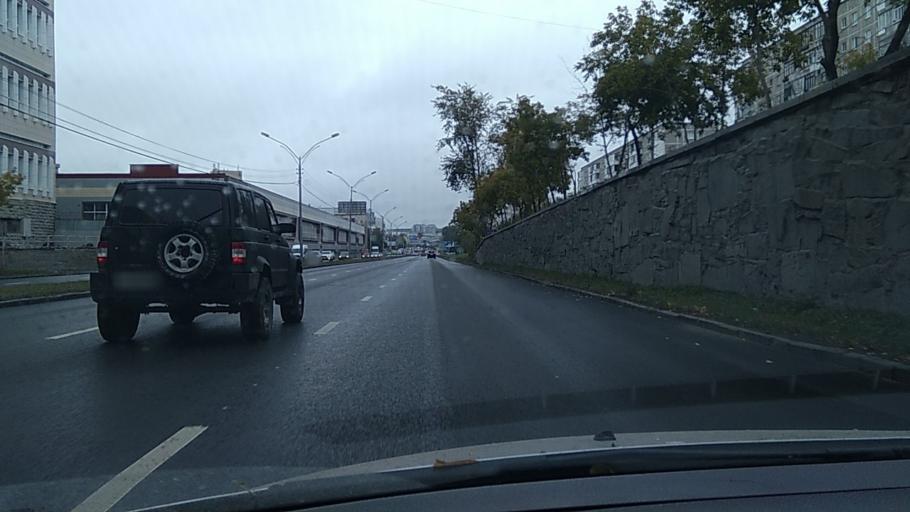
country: RU
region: Sverdlovsk
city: Sovkhoznyy
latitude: 56.8152
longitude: 60.5528
